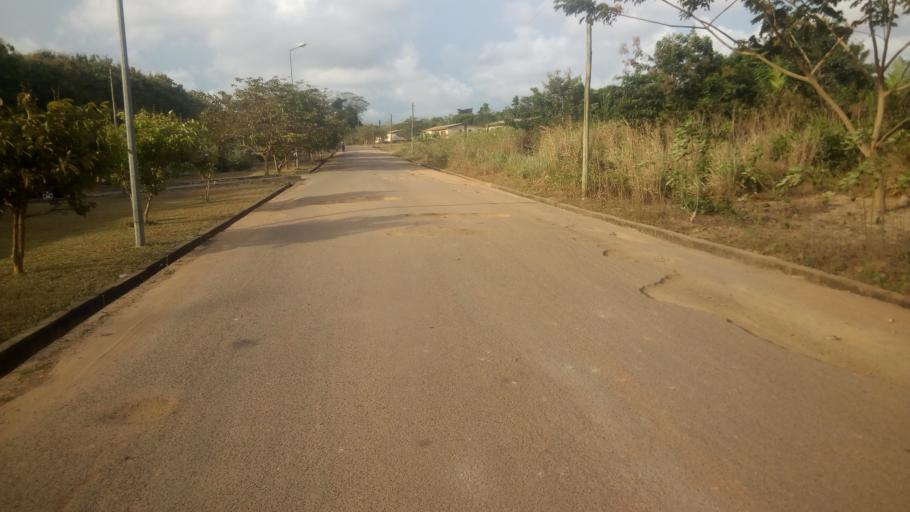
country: GH
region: Central
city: Cape Coast
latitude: 5.1240
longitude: -1.2955
